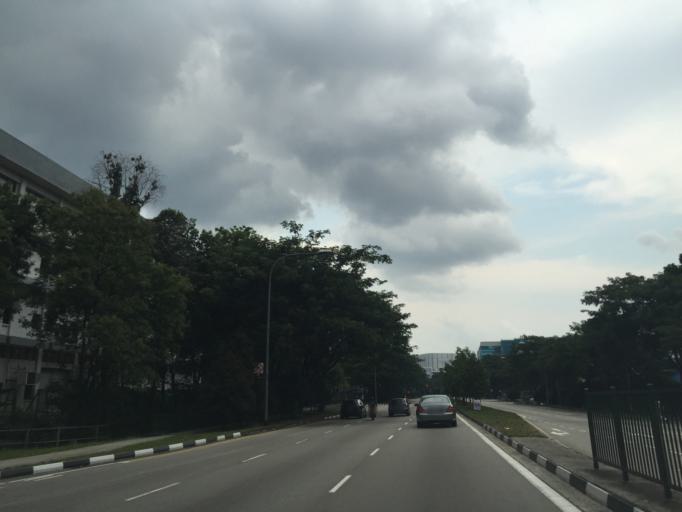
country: MY
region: Johor
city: Johor Bahru
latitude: 1.3272
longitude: 103.6966
